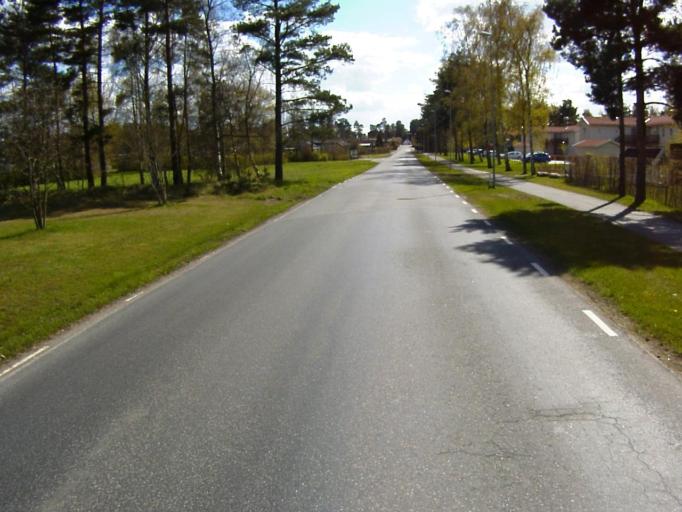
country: SE
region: Skane
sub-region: Kristianstads Kommun
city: Norra Asum
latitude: 56.0086
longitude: 14.0897
